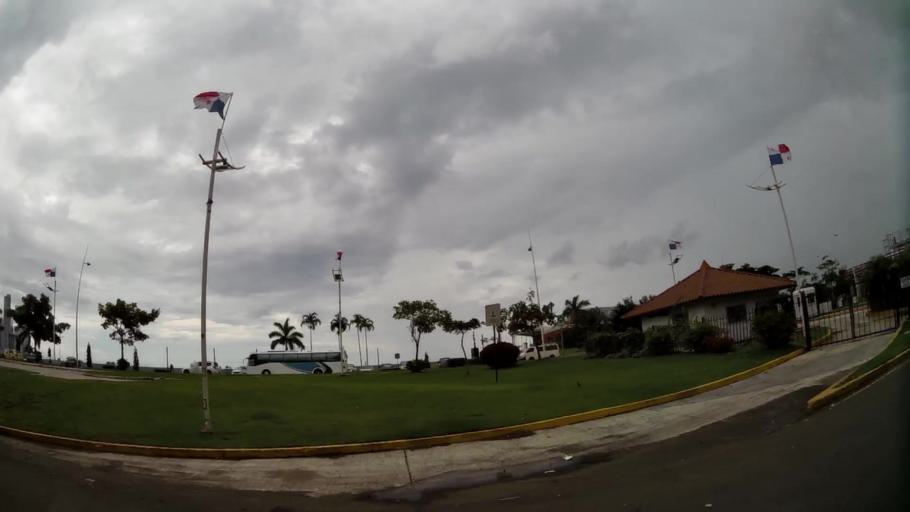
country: PA
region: Panama
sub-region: Distrito de Panama
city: Ancon
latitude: 8.9635
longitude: -79.5354
